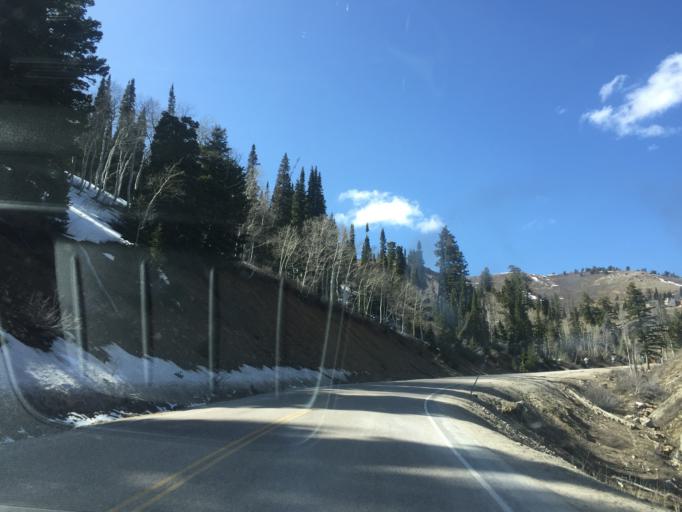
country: US
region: Utah
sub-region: Weber County
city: Wolf Creek
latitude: 41.3738
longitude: -111.7823
